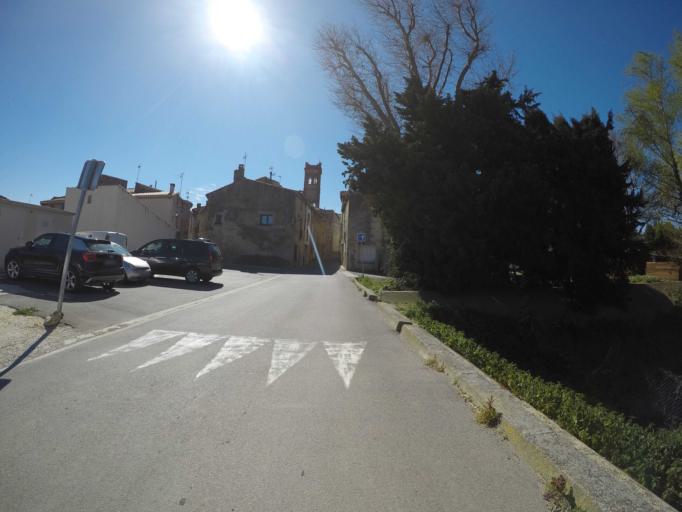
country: FR
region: Languedoc-Roussillon
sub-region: Departement des Pyrenees-Orientales
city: Millas
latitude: 42.6951
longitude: 2.6658
